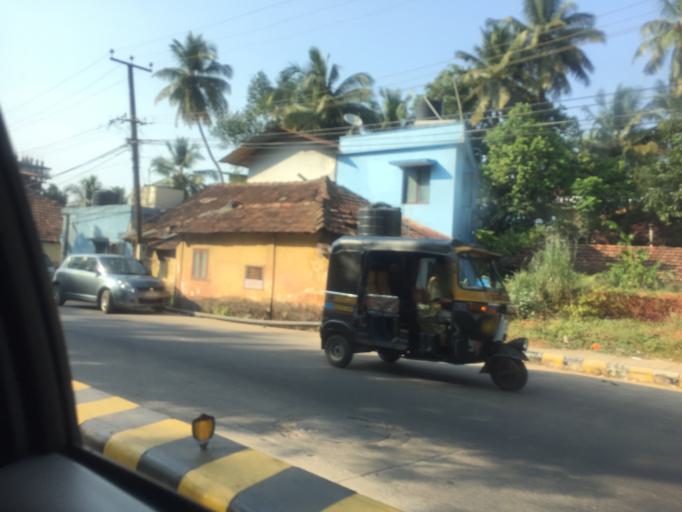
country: IN
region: Karnataka
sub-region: Dakshina Kannada
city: Ullal
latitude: 12.8513
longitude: 74.8439
